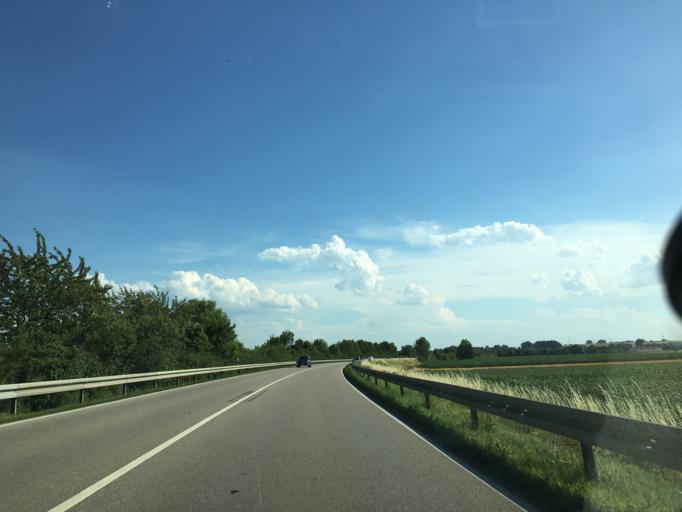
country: DE
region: Bavaria
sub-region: Upper Bavaria
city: Stammham
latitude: 48.3164
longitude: 11.8835
